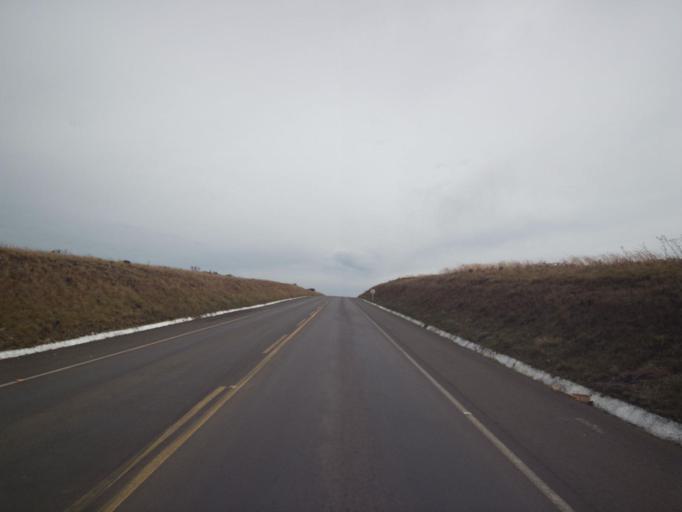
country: BR
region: Parana
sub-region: Palmas
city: Palmas
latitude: -26.7158
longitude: -51.6156
